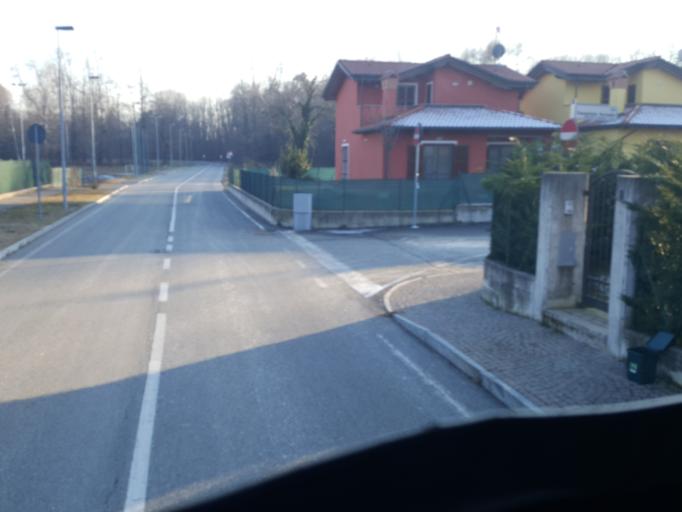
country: IT
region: Piedmont
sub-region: Provincia di Novara
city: Varallo Pombia
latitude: 45.6862
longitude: 8.6273
